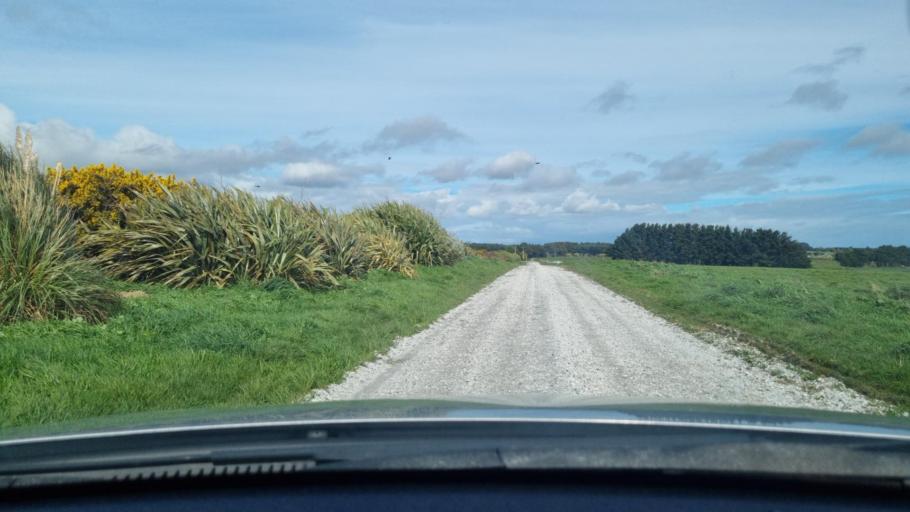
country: NZ
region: Southland
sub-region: Invercargill City
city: Invercargill
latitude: -46.4560
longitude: 168.3858
